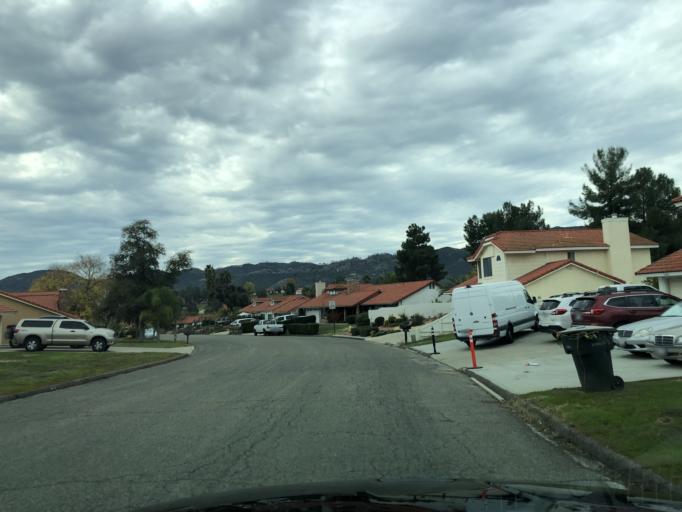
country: US
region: California
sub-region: Riverside County
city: Wildomar
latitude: 33.6192
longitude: -117.2843
